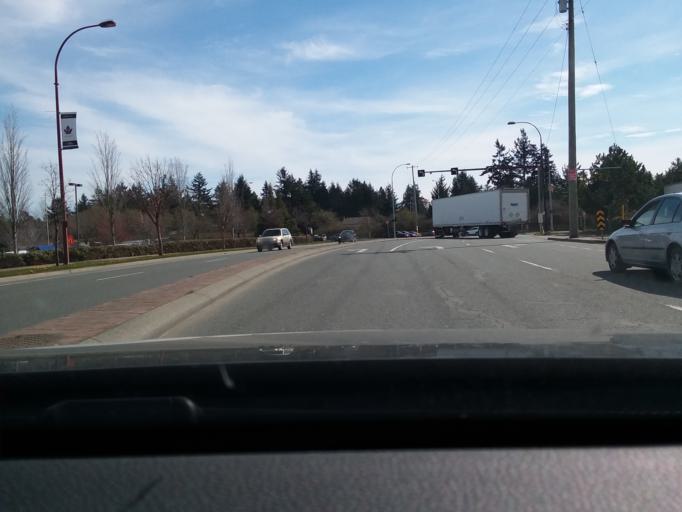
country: CA
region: British Columbia
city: Langford
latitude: 48.4420
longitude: -123.5034
